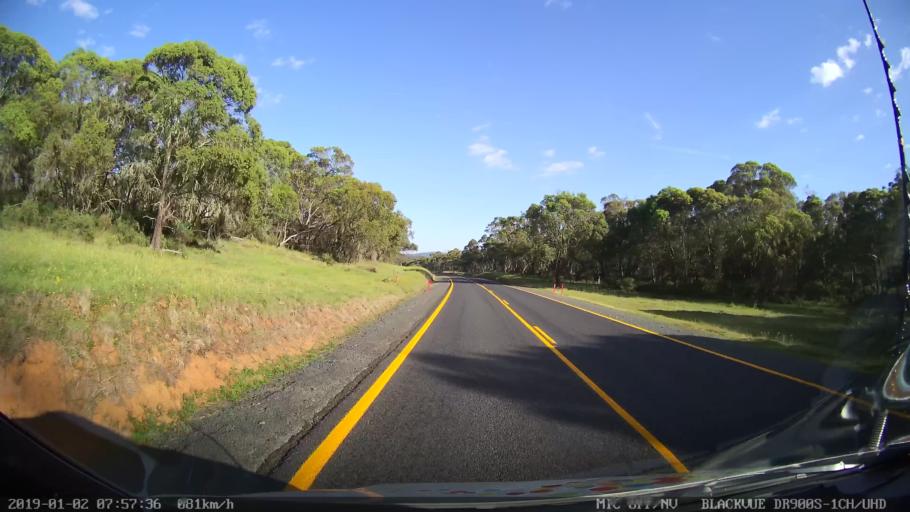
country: AU
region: New South Wales
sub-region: Tumut Shire
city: Tumut
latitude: -35.6618
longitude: 148.4729
